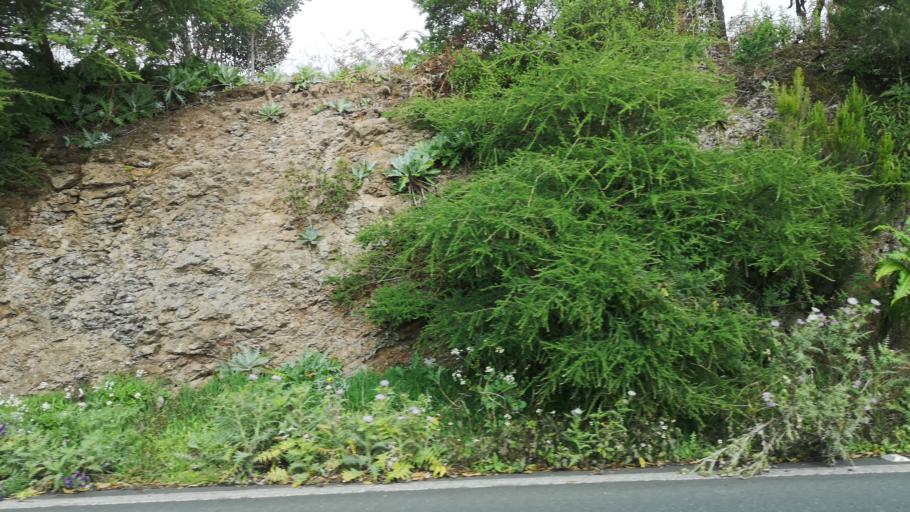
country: ES
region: Canary Islands
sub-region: Provincia de Santa Cruz de Tenerife
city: Alajero
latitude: 28.1084
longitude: -17.2220
